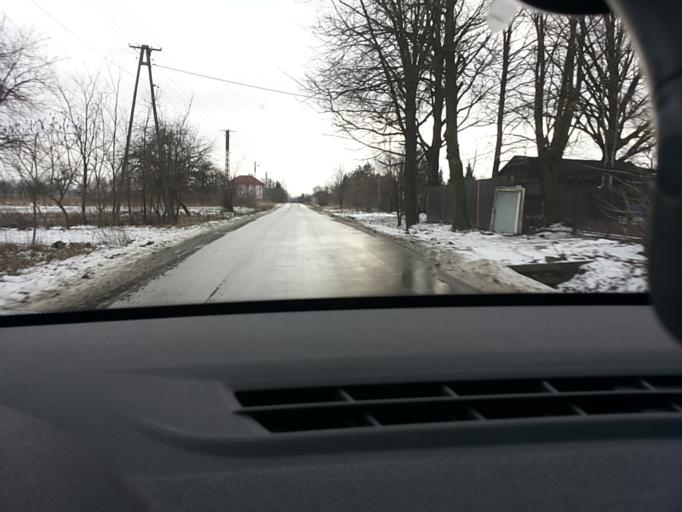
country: PL
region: Lodz Voivodeship
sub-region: Powiat skierniewicki
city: Makow
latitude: 51.9980
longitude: 20.0764
